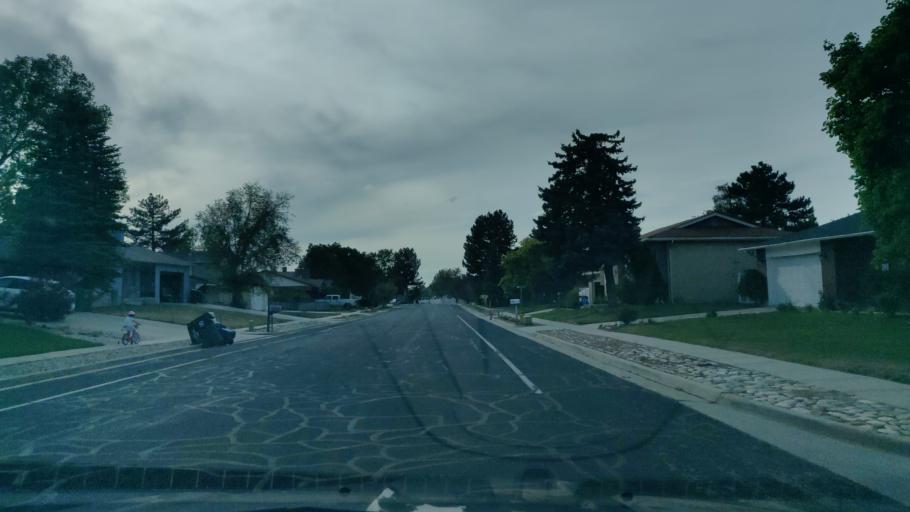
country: US
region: Utah
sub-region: Salt Lake County
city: Little Cottonwood Creek Valley
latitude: 40.6157
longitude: -111.8358
